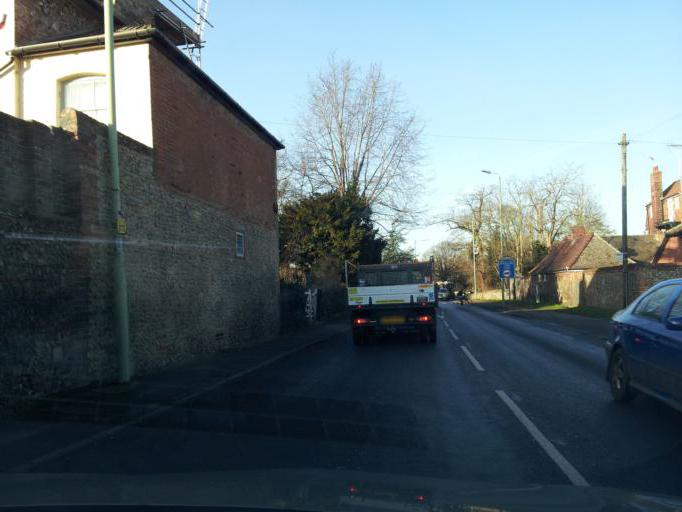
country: GB
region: England
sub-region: Suffolk
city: Bury St Edmunds
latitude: 52.2350
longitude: 0.7263
